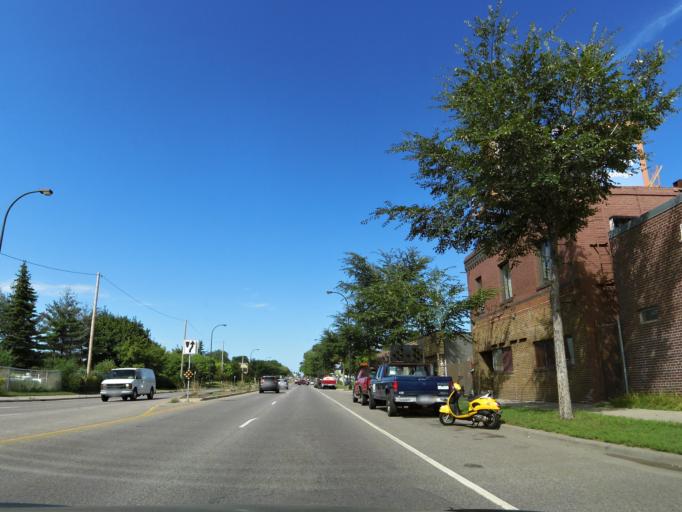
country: US
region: Minnesota
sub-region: Anoka County
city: Columbia Heights
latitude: 45.0206
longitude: -93.2473
